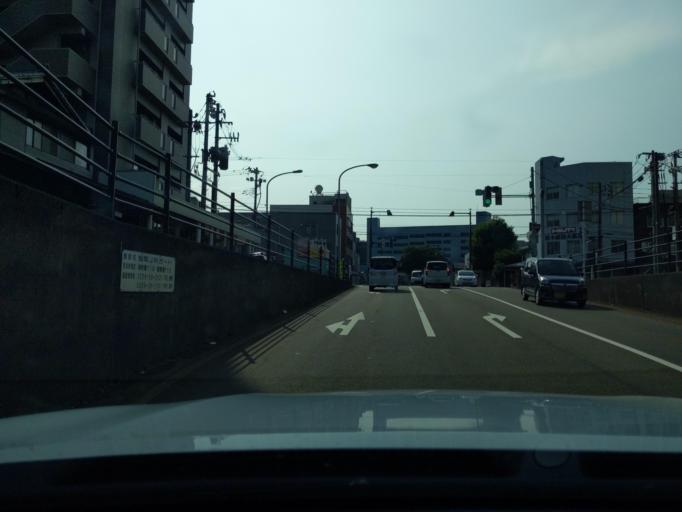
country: JP
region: Niigata
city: Nagaoka
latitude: 37.4430
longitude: 138.8515
